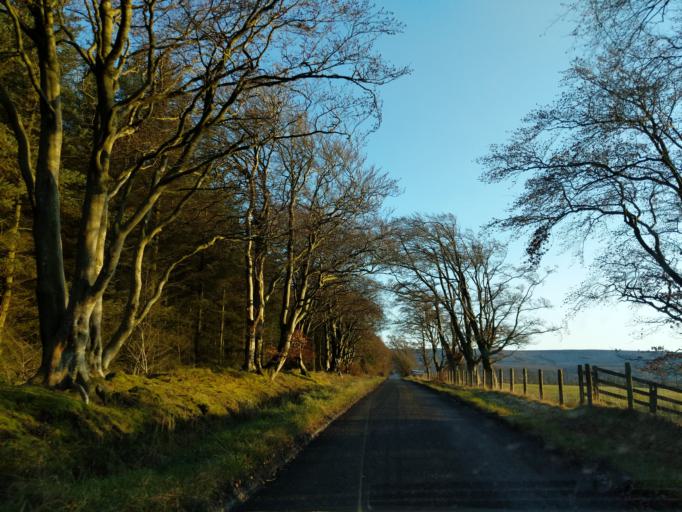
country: GB
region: Scotland
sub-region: Edinburgh
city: Balerno
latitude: 55.8575
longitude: -3.3634
